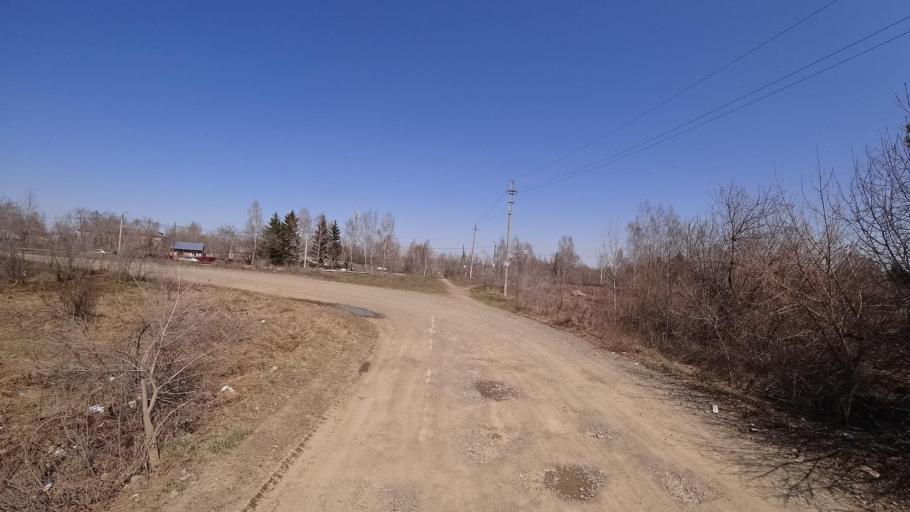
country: RU
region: Khabarovsk Krai
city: Khurba
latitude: 50.4074
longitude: 136.8923
